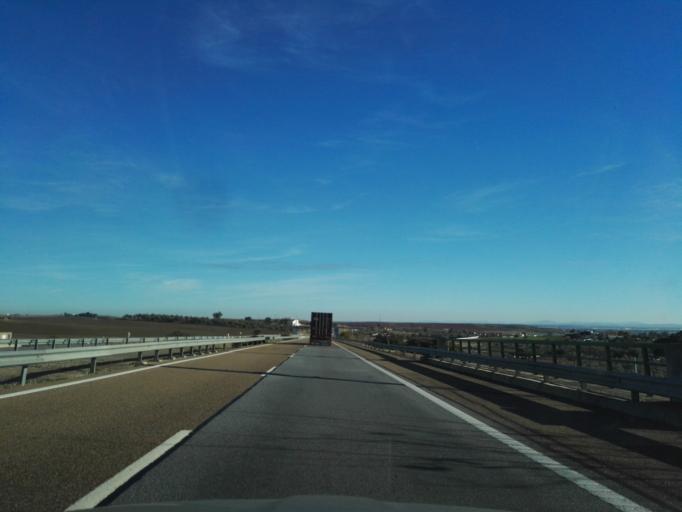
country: PT
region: Portalegre
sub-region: Elvas
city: Elvas
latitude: 38.8986
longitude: -7.1292
